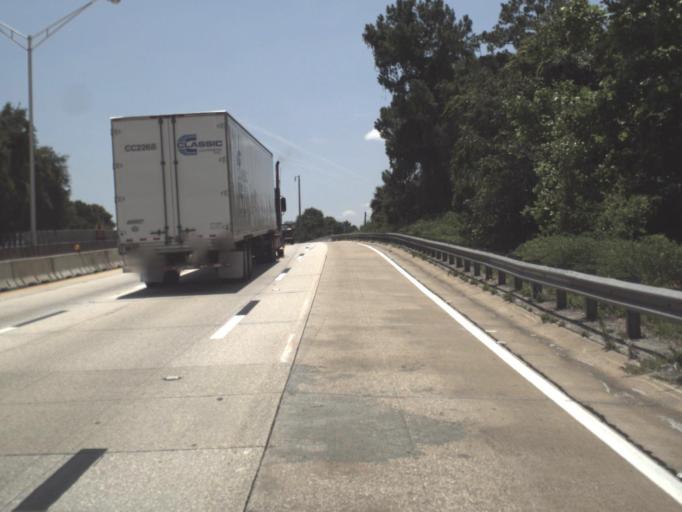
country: US
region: Florida
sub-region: Duval County
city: Jacksonville
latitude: 30.3011
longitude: -81.6405
